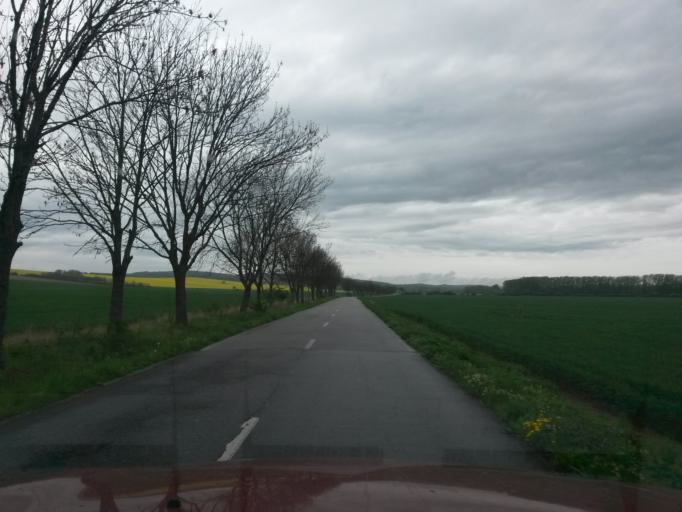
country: HU
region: Borsod-Abauj-Zemplen
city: Gonc
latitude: 48.5447
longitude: 21.2188
